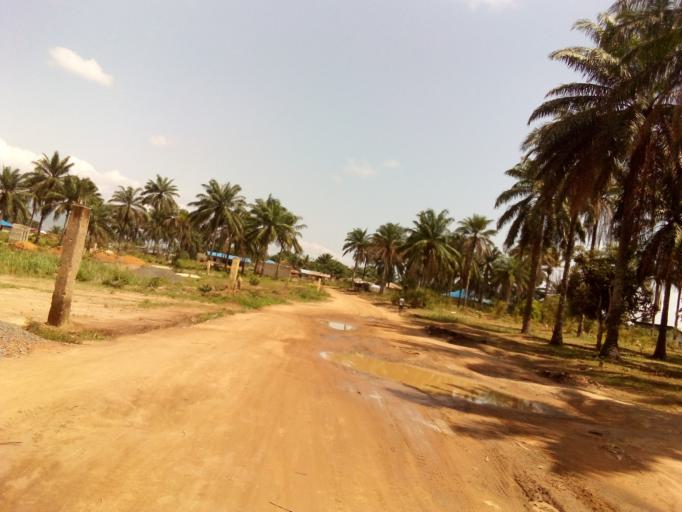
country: SL
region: Western Area
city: Waterloo
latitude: 8.3486
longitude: -13.0167
